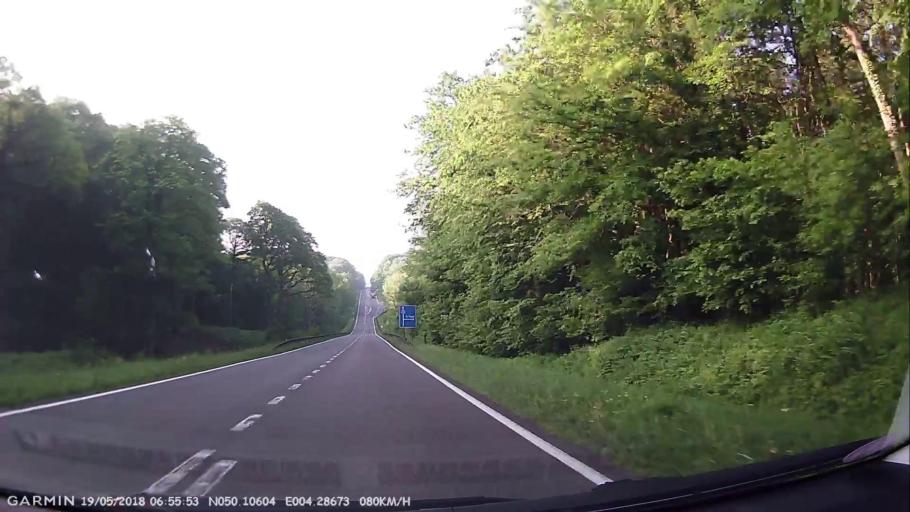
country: BE
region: Wallonia
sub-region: Province du Hainaut
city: Froidchapelle
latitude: 50.1058
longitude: 4.2868
